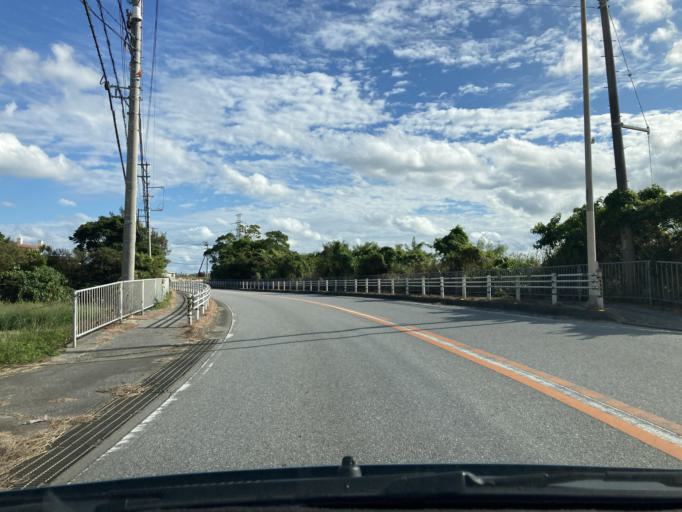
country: JP
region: Okinawa
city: Ishikawa
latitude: 26.4260
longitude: 127.8078
